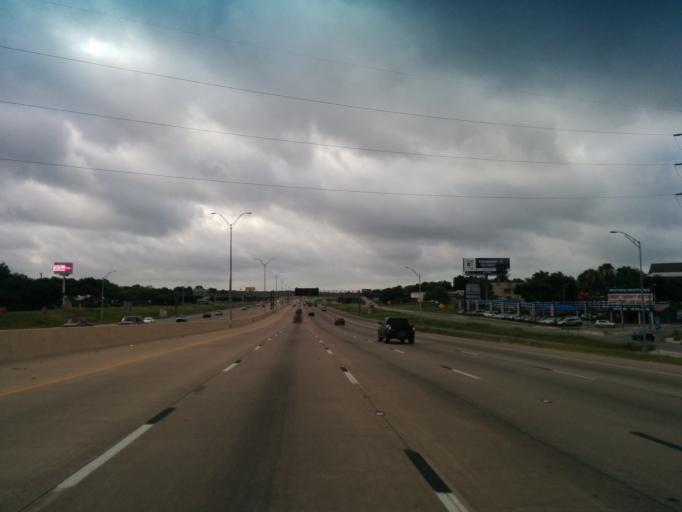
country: US
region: Texas
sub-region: Bexar County
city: Balcones Heights
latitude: 29.4803
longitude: -98.5247
